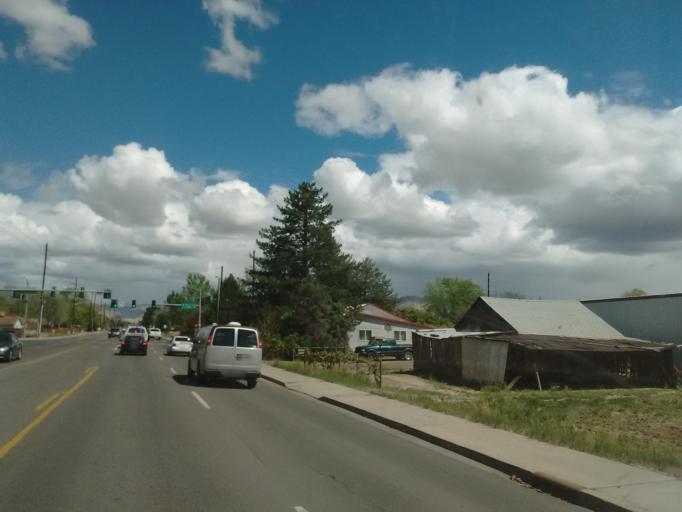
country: US
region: Colorado
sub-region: Mesa County
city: Fruitvale
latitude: 39.0838
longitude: -108.4965
